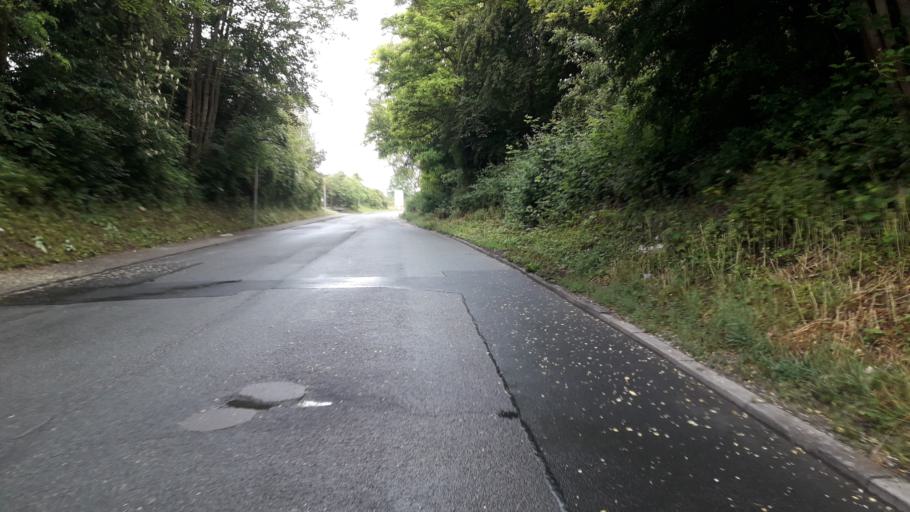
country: DE
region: North Rhine-Westphalia
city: Warburg
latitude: 51.4943
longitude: 9.1595
